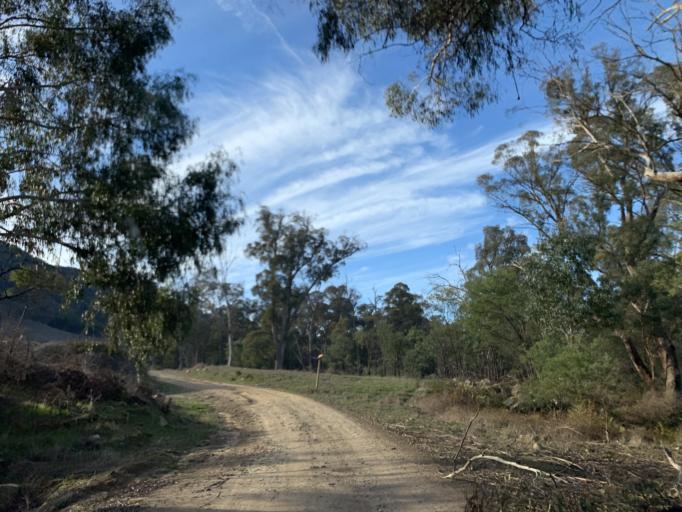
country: AU
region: Victoria
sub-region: Mansfield
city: Mansfield
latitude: -36.9322
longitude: 146.0933
